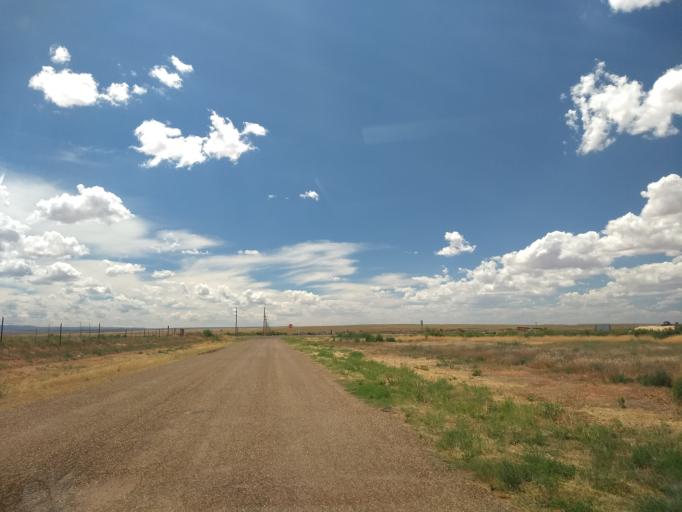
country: US
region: Arizona
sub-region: Coconino County
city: Fredonia
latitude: 36.9397
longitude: -112.5179
